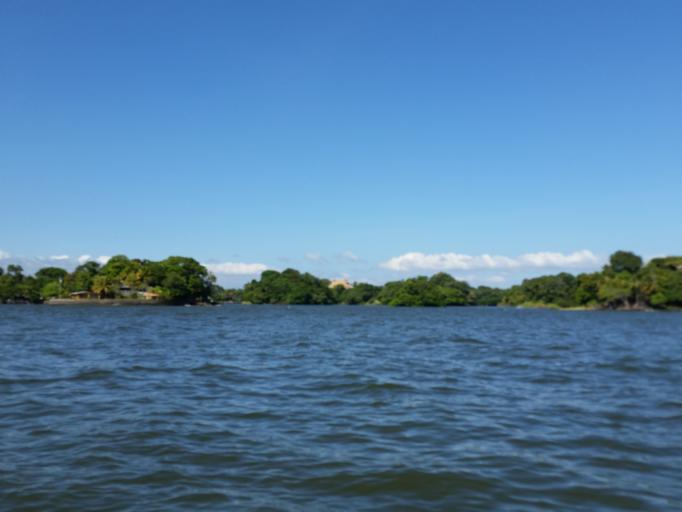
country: NI
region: Granada
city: Granada
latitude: 11.9124
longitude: -85.9020
